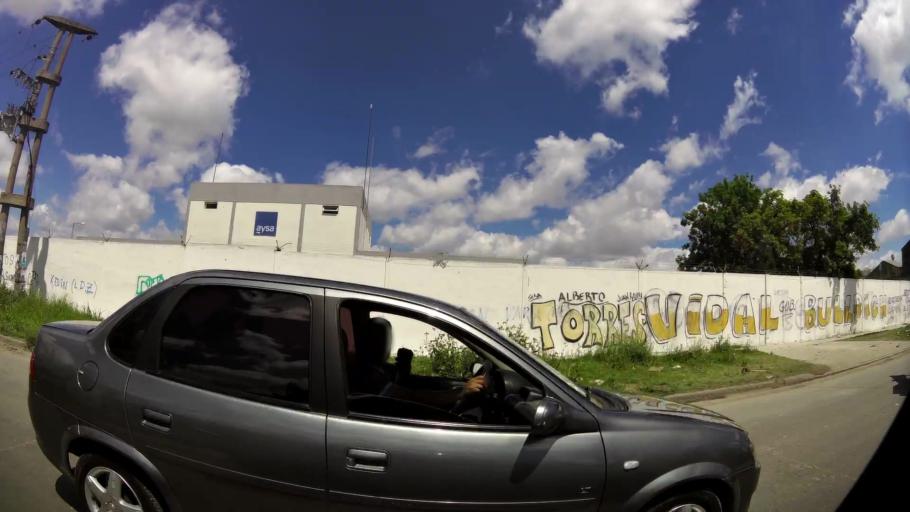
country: AR
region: Buenos Aires F.D.
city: Villa Lugano
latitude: -34.6869
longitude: -58.4388
